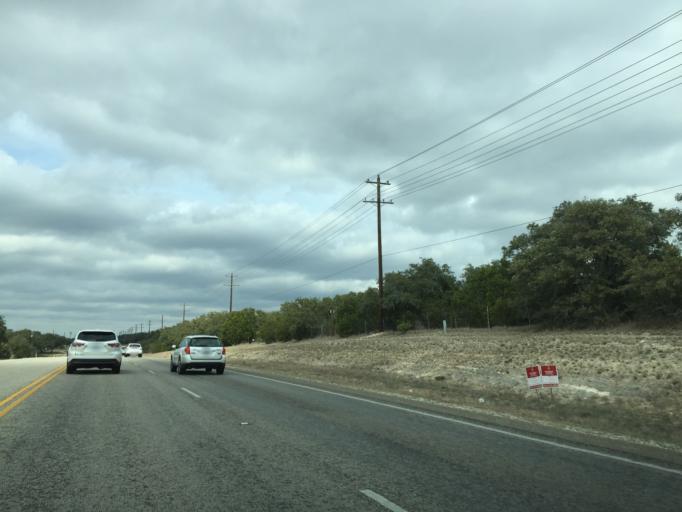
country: US
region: Texas
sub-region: Travis County
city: Briarcliff
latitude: 30.3952
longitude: -98.0877
